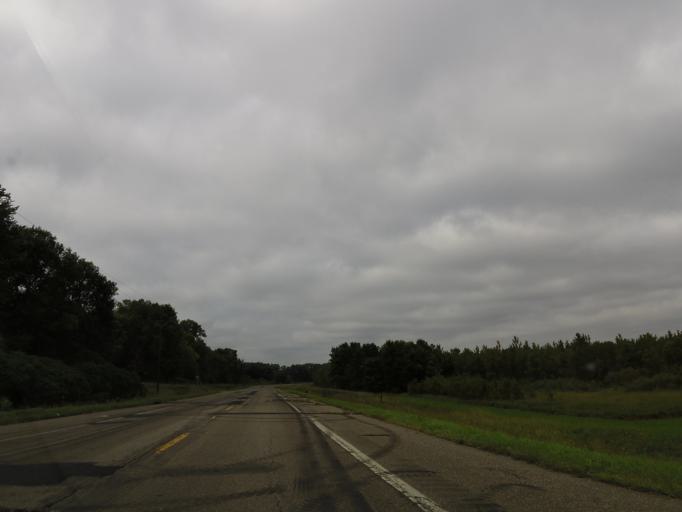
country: US
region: Minnesota
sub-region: Chippewa County
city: Montevideo
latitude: 44.8977
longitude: -95.6772
